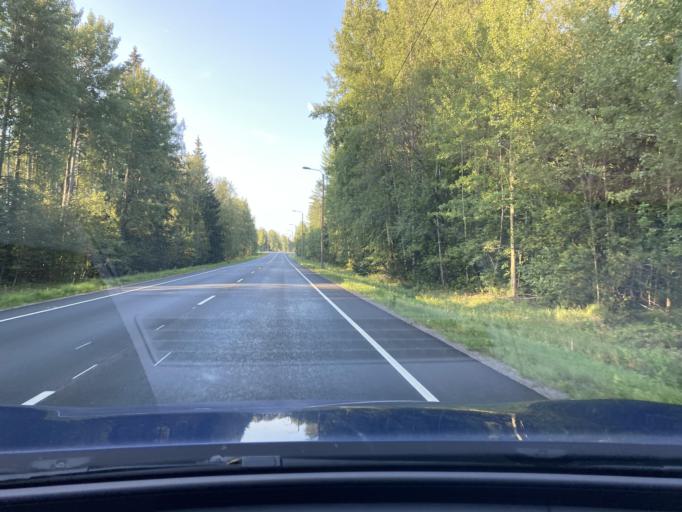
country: FI
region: Kymenlaakso
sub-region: Kouvola
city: Kouvola
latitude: 60.8909
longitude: 26.6045
